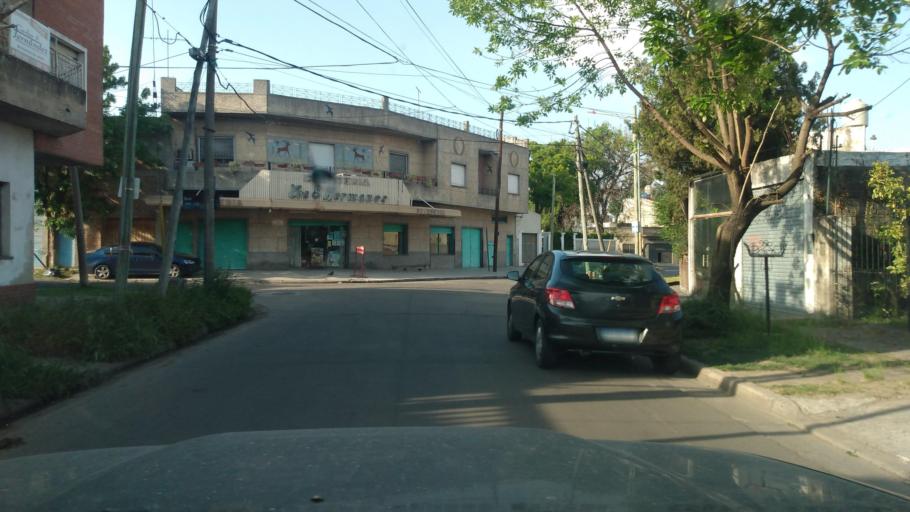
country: AR
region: Buenos Aires
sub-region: Partido de Moron
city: Moron
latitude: -34.6343
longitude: -58.6192
